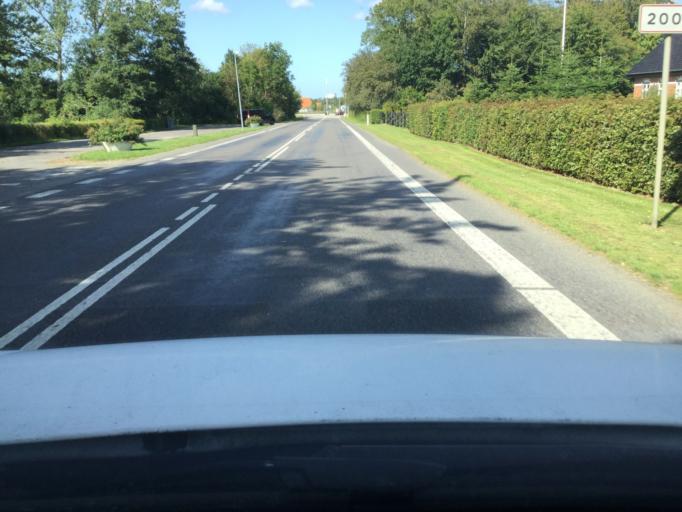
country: DK
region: Zealand
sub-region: Lolland Kommune
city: Nakskov
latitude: 54.8006
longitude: 11.2732
